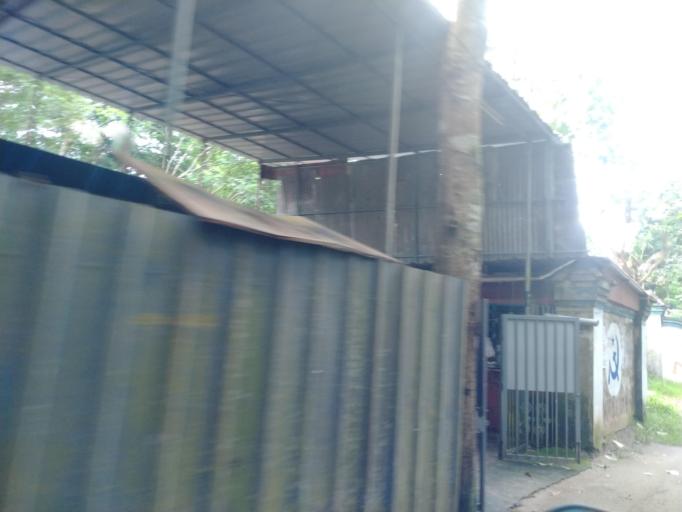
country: IN
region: Kerala
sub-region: Alappuzha
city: Shertallai
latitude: 9.6181
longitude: 76.3622
